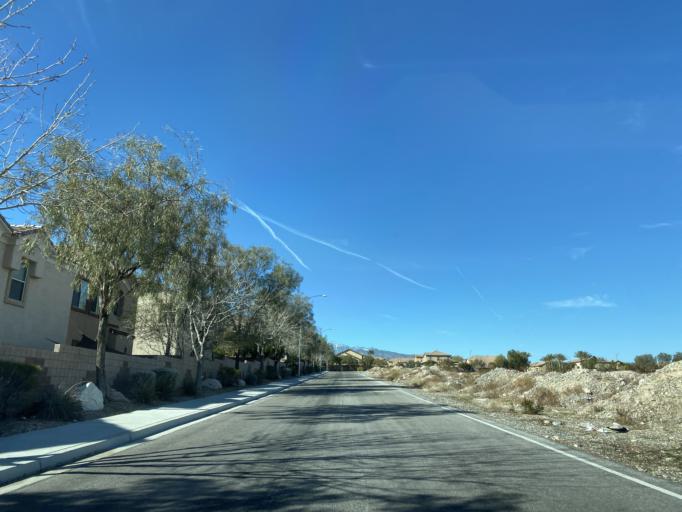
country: US
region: Nevada
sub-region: Clark County
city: Summerlin South
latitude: 36.3011
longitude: -115.3037
